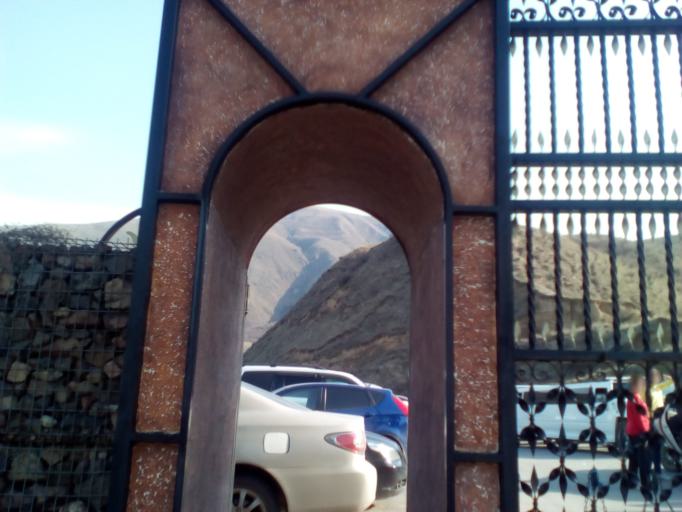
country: KZ
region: Almaty Oblysy
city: Burunday
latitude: 43.1517
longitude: 76.5711
